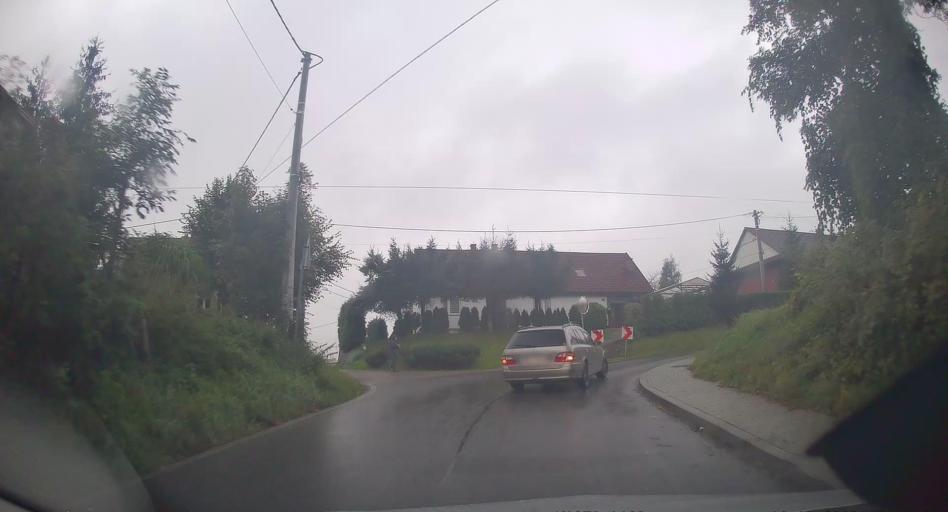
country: PL
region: Lesser Poland Voivodeship
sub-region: Powiat krakowski
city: Ochojno
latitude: 49.9590
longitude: 19.9996
